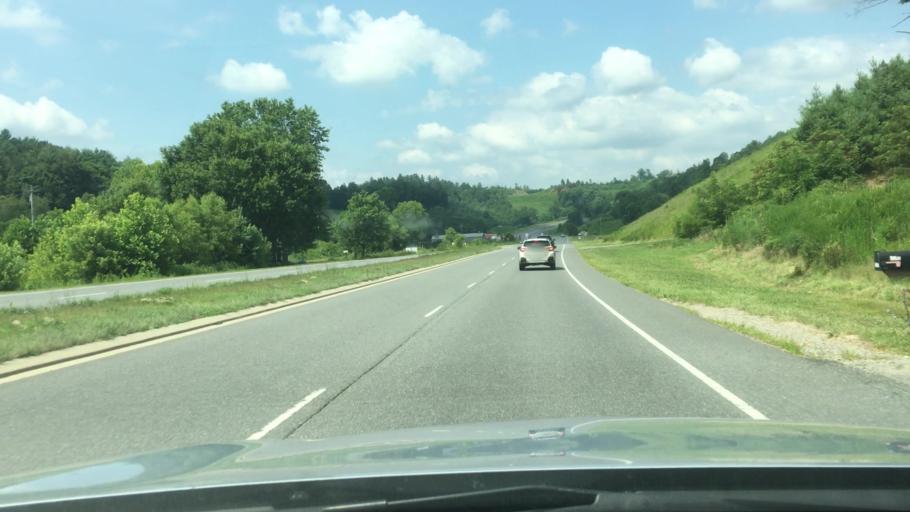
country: US
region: North Carolina
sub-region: Madison County
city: Mars Hill
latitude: 35.8436
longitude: -82.5017
